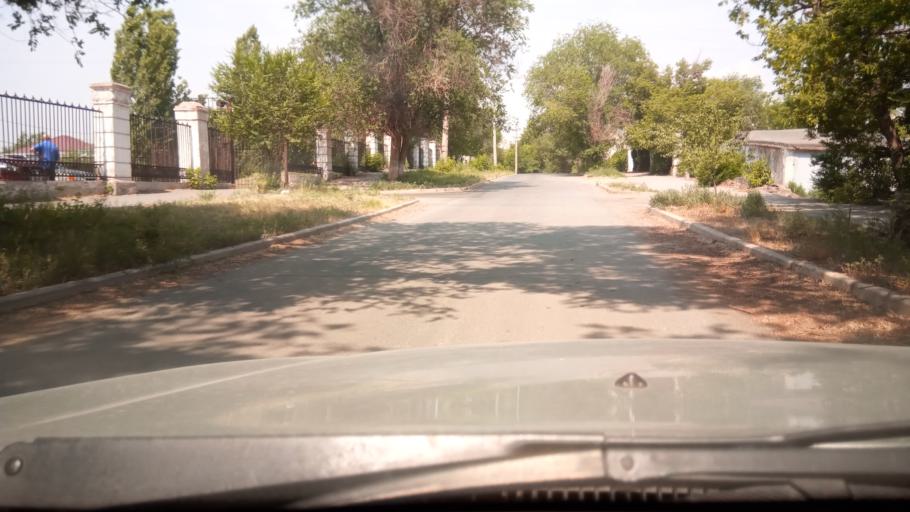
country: RU
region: Orenburg
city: Novotroitsk
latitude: 51.1953
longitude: 58.3326
